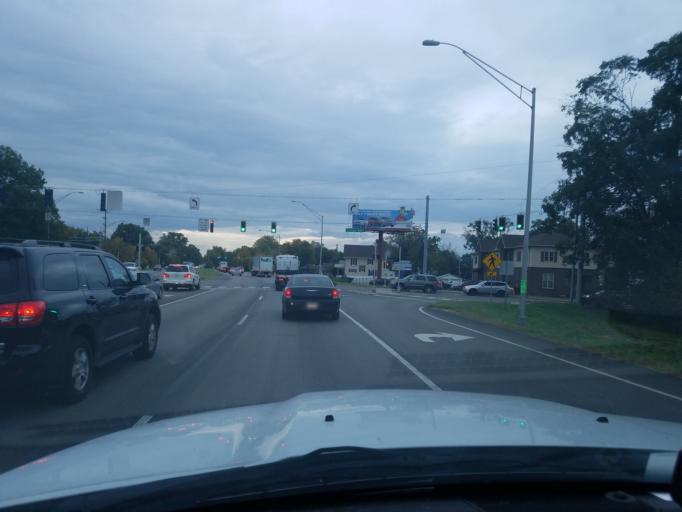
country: US
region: Indiana
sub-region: Vanderburgh County
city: Evansville
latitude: 37.9705
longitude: -87.5441
